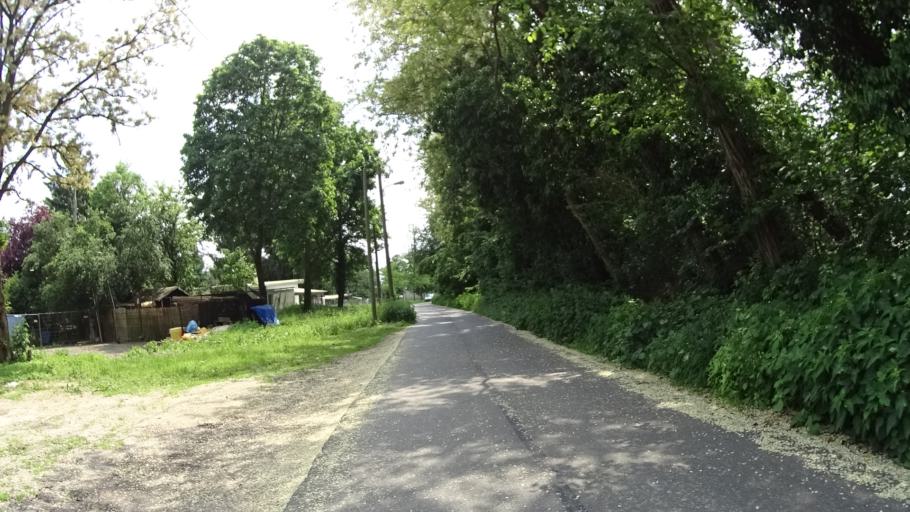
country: DE
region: Baden-Wuerttemberg
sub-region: Karlsruhe Region
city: Rheinstetten
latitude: 48.9906
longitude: 8.3310
